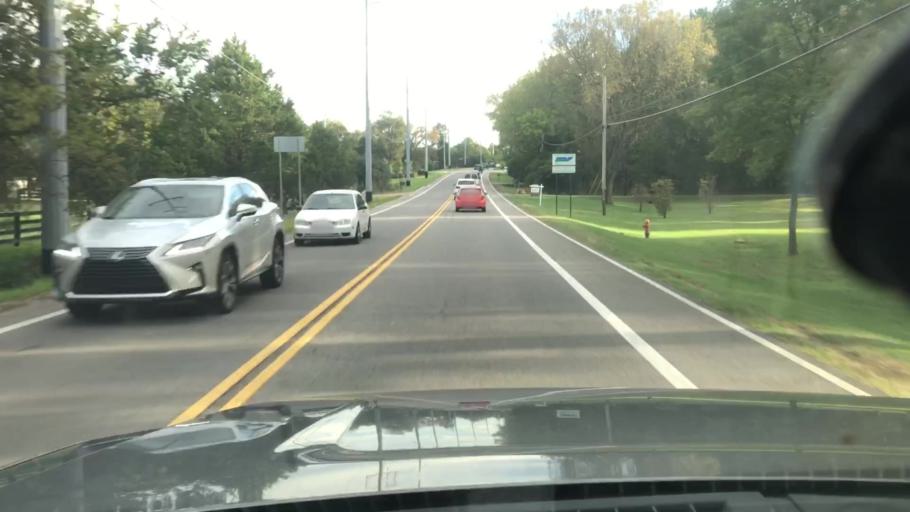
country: US
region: Tennessee
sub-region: Davidson County
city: Forest Hills
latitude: 36.0575
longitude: -86.8547
